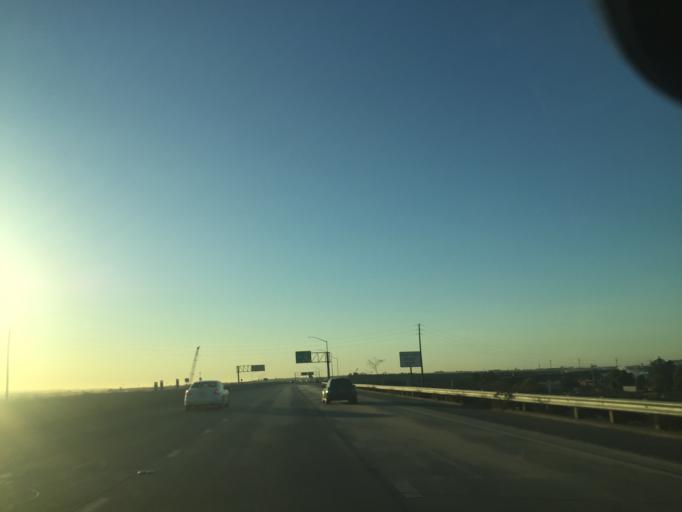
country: MX
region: Baja California
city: Tijuana
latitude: 32.5640
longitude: -116.9410
